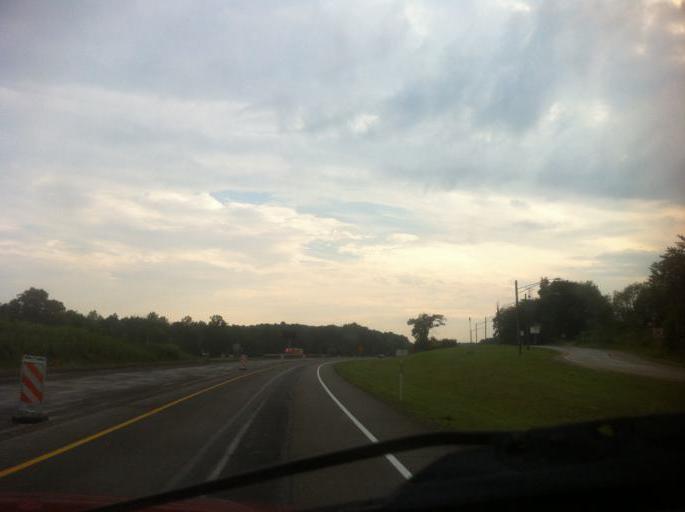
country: US
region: Pennsylvania
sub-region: Clarion County
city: Knox
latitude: 41.1977
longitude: -79.4990
